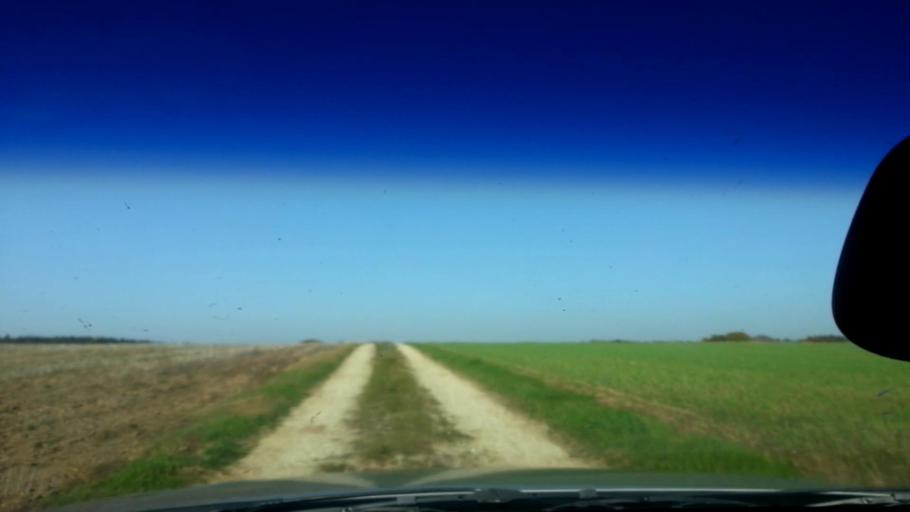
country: DE
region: Bavaria
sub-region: Upper Franconia
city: Wonsees
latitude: 49.9648
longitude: 11.2688
